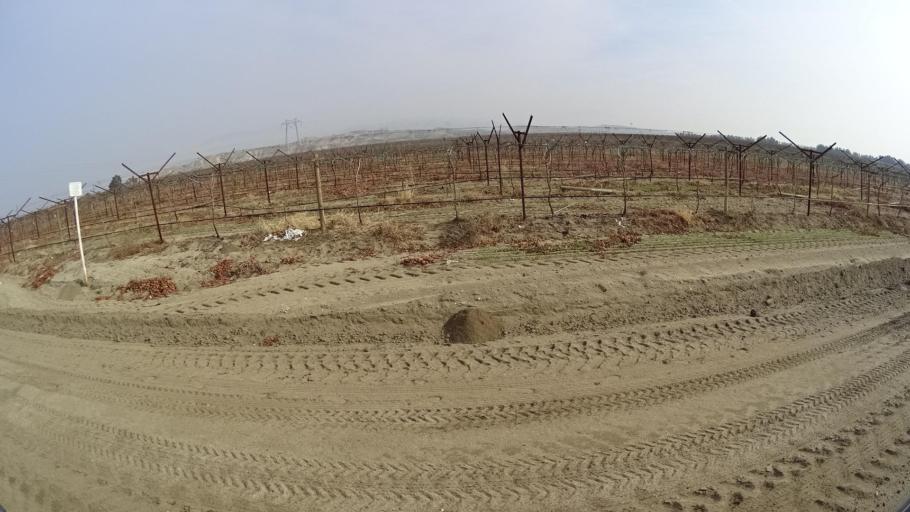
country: US
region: California
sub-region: Kern County
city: Arvin
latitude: 35.1187
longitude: -118.8506
